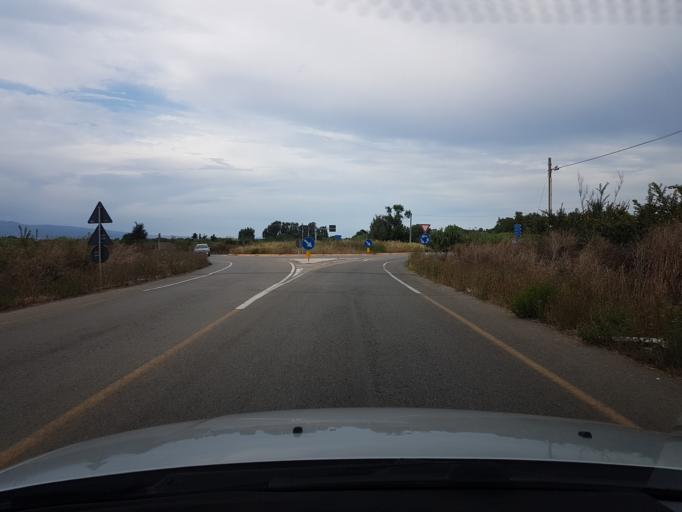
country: IT
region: Sardinia
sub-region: Provincia di Oristano
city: Nuraxinieddu
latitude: 39.9466
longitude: 8.6048
